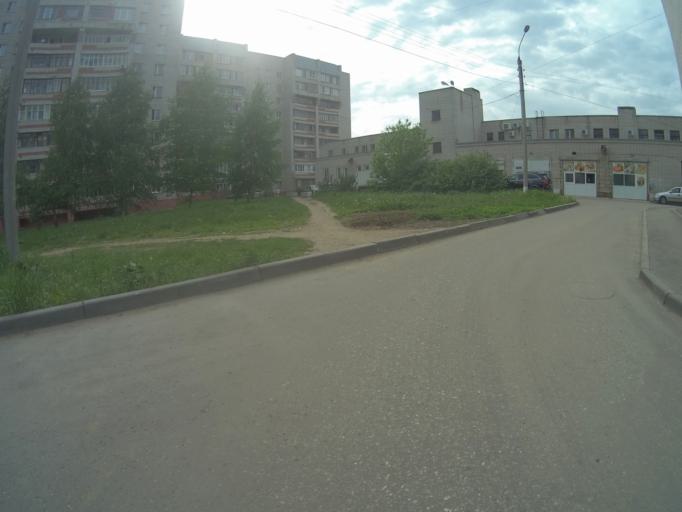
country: RU
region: Vladimir
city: Kommunar
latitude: 56.1664
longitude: 40.4626
